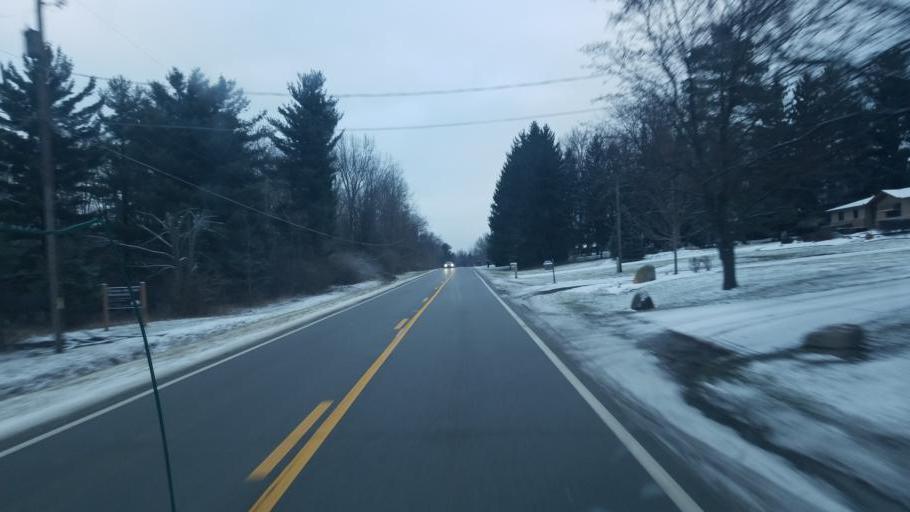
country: US
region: Ohio
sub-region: Franklin County
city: Huber Ridge
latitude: 40.1117
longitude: -82.8722
